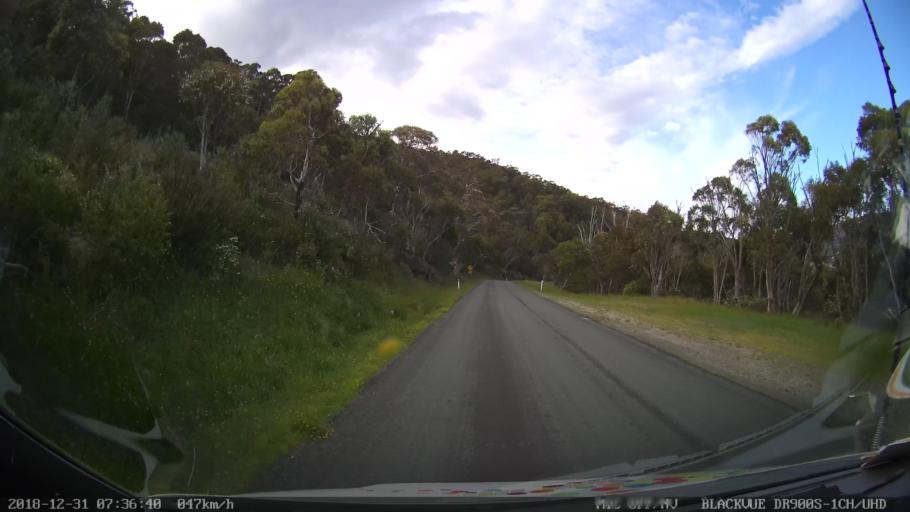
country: AU
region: New South Wales
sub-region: Snowy River
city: Jindabyne
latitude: -36.3423
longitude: 148.4417
